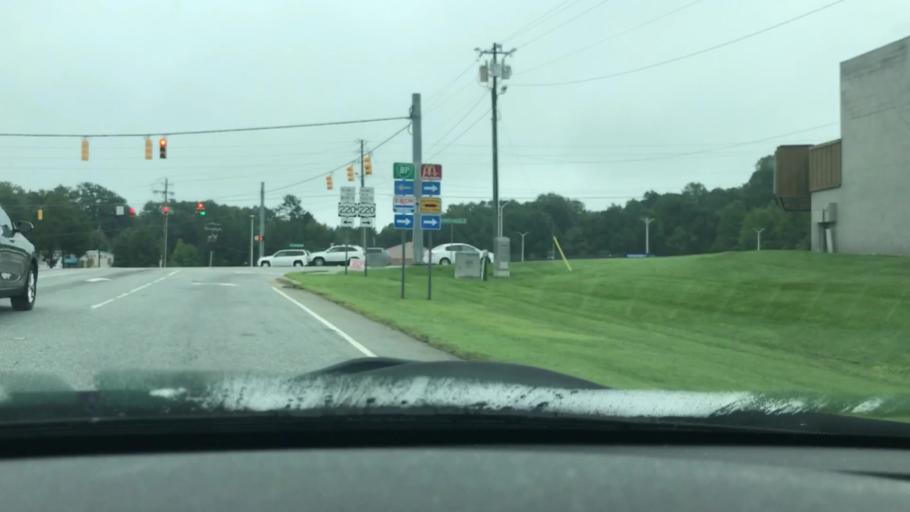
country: US
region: North Carolina
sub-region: Randolph County
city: Asheboro
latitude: 35.7366
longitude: -79.8092
